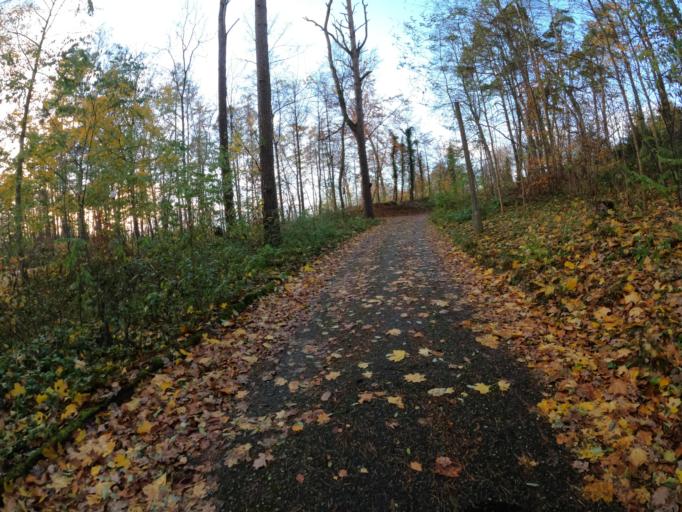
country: PL
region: West Pomeranian Voivodeship
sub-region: Powiat walecki
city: Tuczno
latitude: 53.1906
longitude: 16.1601
